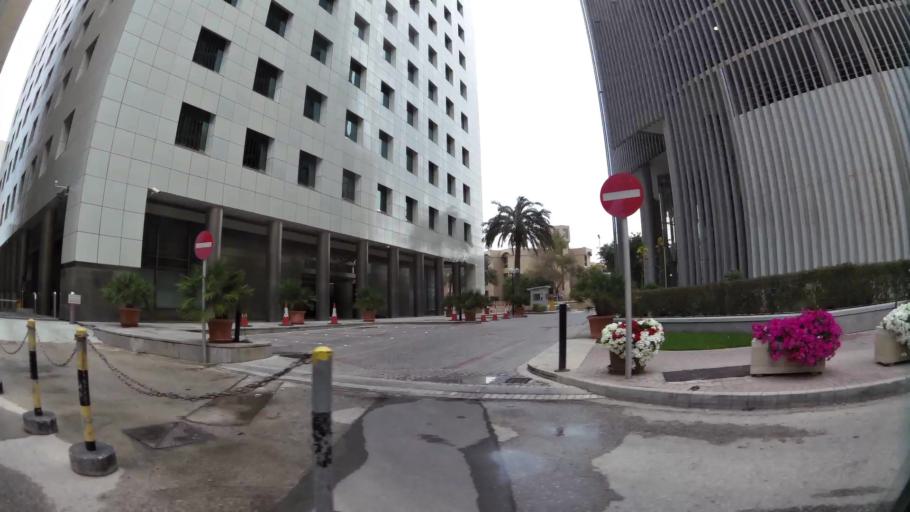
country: BH
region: Muharraq
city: Al Muharraq
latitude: 26.2432
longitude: 50.5891
